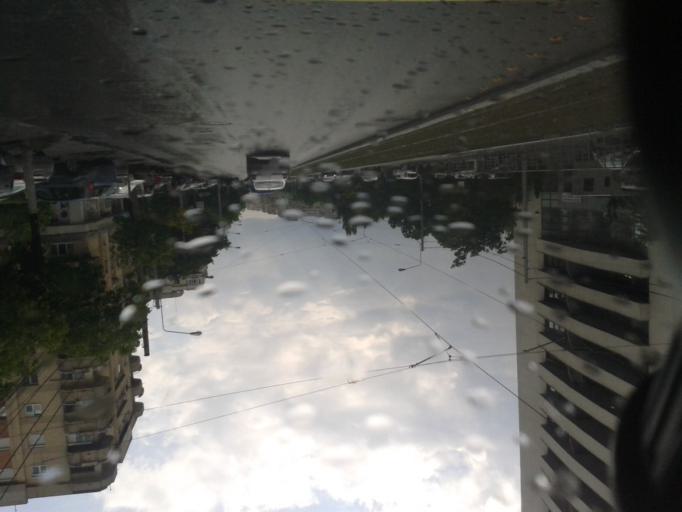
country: RO
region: Prahova
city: Ploiesti
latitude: 44.9465
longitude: 26.0162
